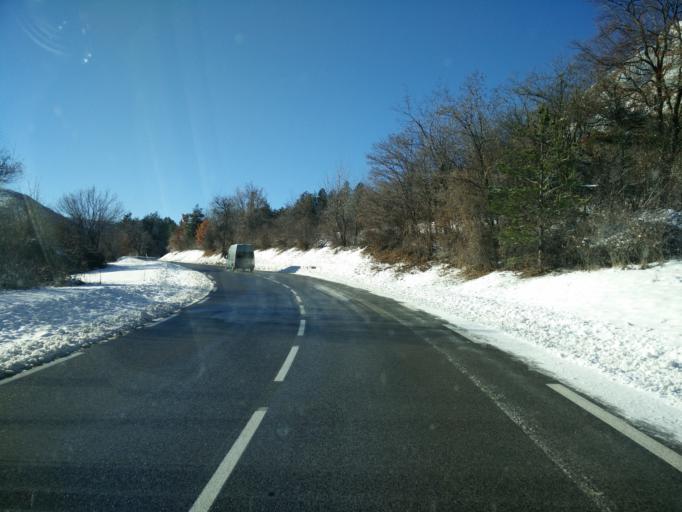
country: FR
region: Provence-Alpes-Cote d'Azur
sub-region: Departement des Alpes-de-Haute-Provence
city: Annot
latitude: 43.9317
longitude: 6.6255
